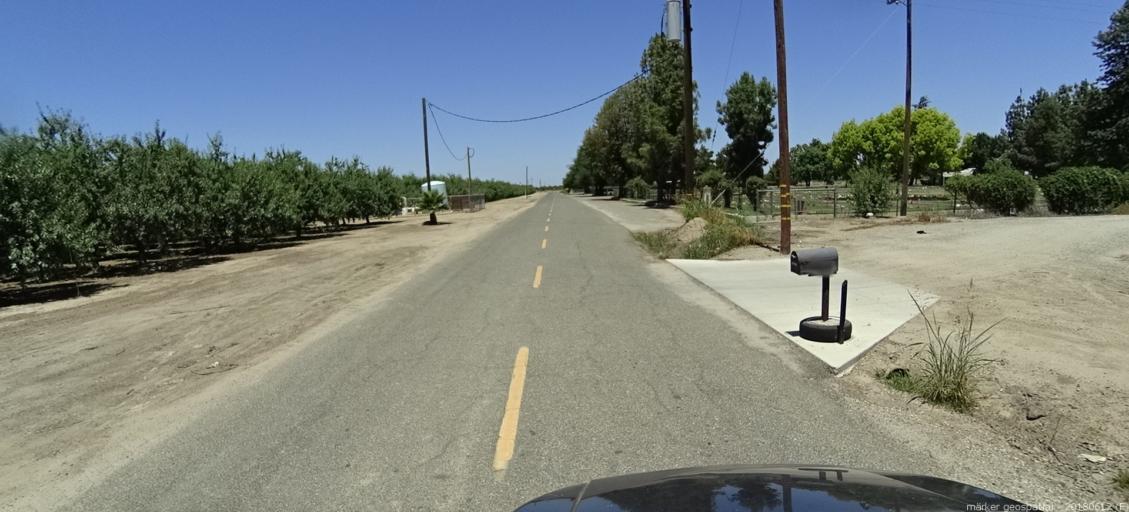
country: US
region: California
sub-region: Madera County
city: Chowchilla
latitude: 37.0868
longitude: -120.2836
